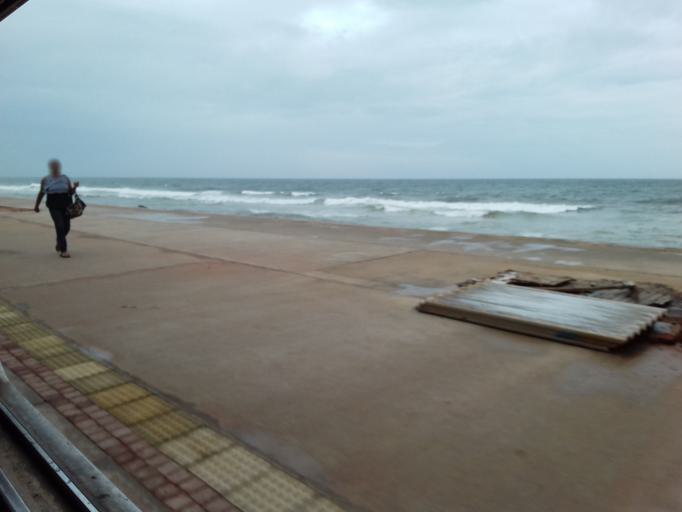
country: LK
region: Western
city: Colombo
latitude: 6.9108
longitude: 79.8483
